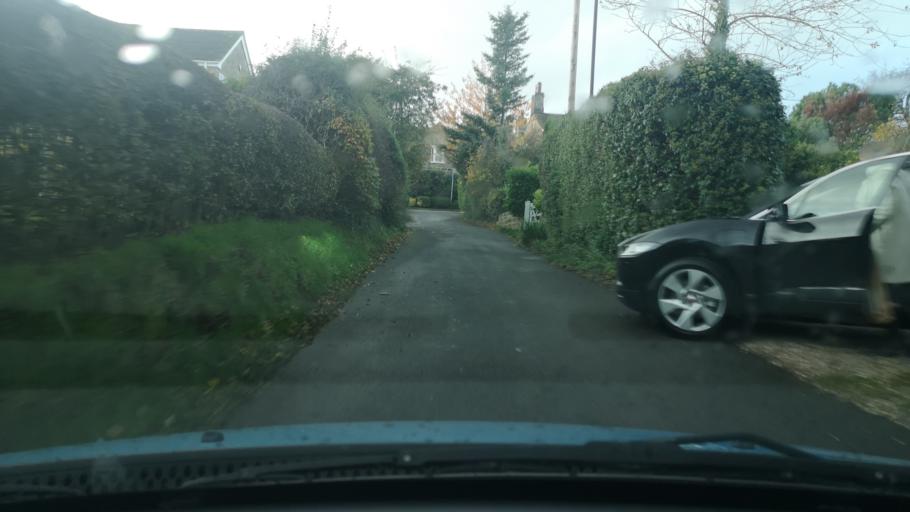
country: GB
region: England
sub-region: City and Borough of Wakefield
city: Woolley
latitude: 53.6148
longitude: -1.5191
